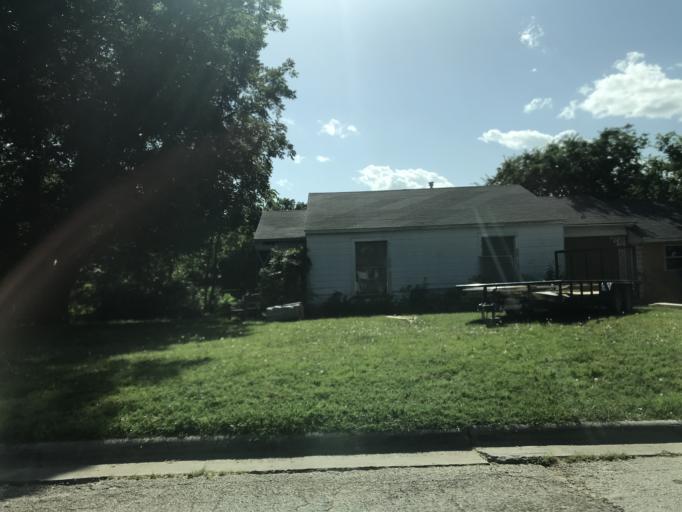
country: US
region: Texas
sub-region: Taylor County
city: Abilene
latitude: 32.4278
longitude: -99.7571
